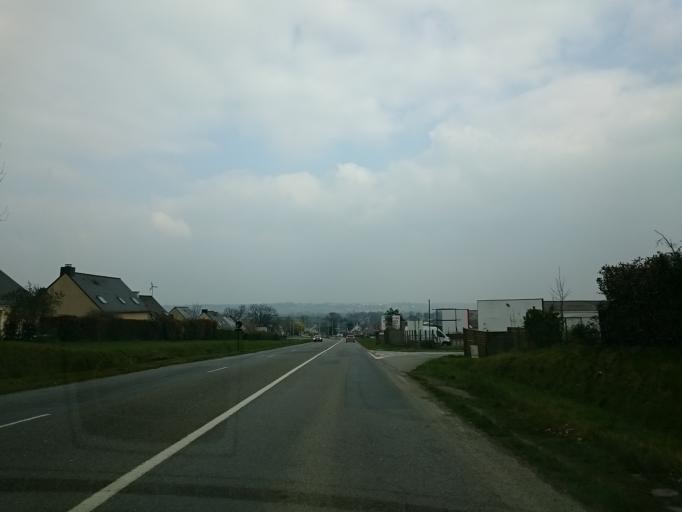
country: FR
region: Brittany
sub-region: Departement d'Ille-et-Vilaine
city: Bain-de-Bretagne
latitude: 47.8490
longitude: -1.6825
